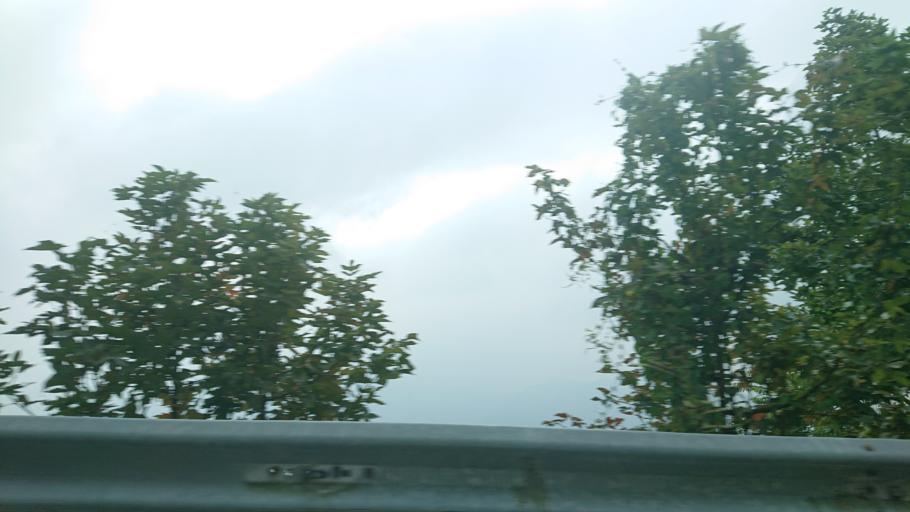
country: TW
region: Taiwan
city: Lugu
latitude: 23.6020
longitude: 120.7034
